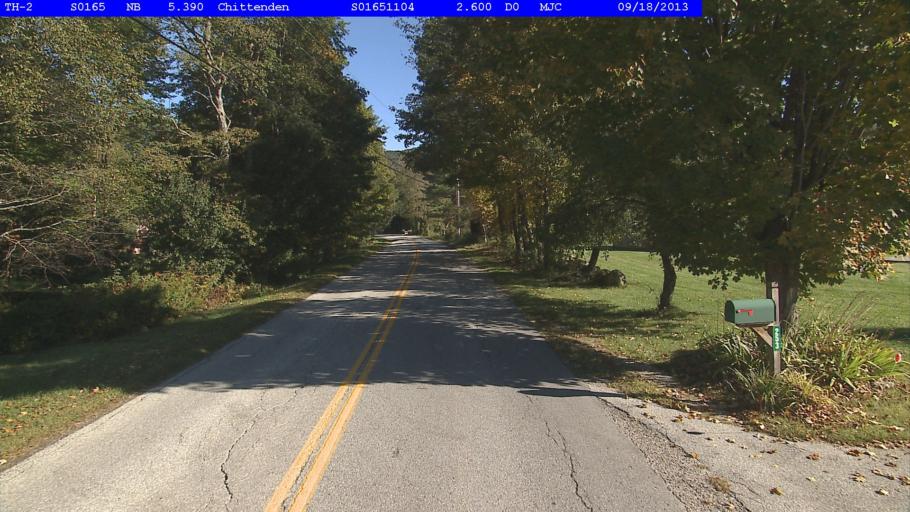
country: US
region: Vermont
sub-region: Rutland County
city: Rutland
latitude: 43.7131
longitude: -72.9613
